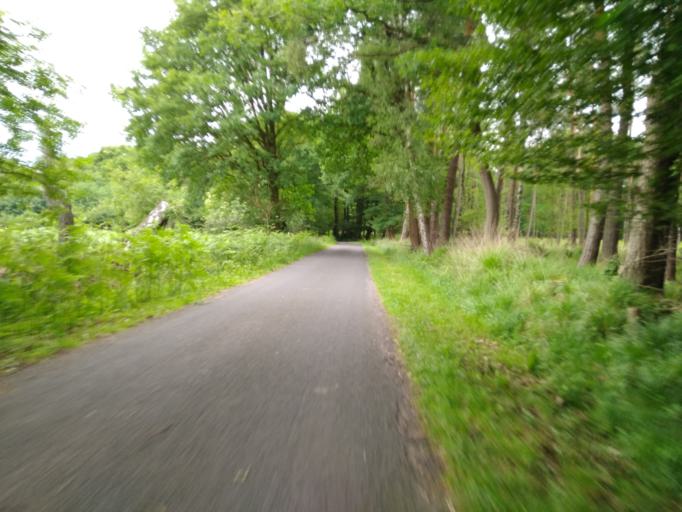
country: DE
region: North Rhine-Westphalia
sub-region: Regierungsbezirk Dusseldorf
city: Hunxe
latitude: 51.6380
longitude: 6.8296
